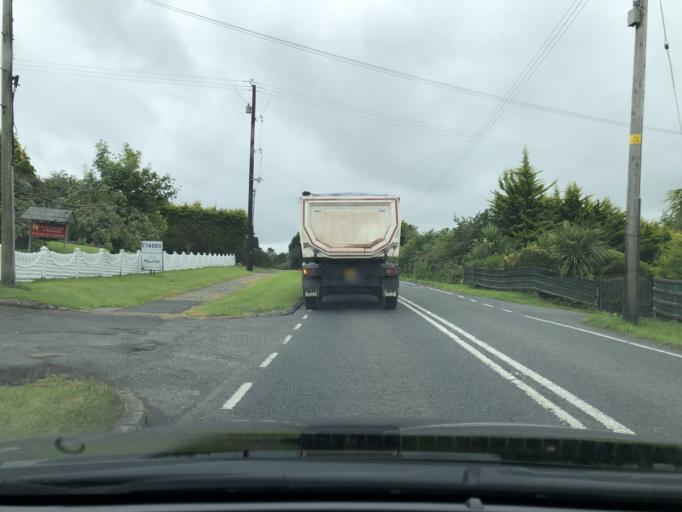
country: GB
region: Northern Ireland
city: Ballynahinch
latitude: 54.3662
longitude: -5.8607
